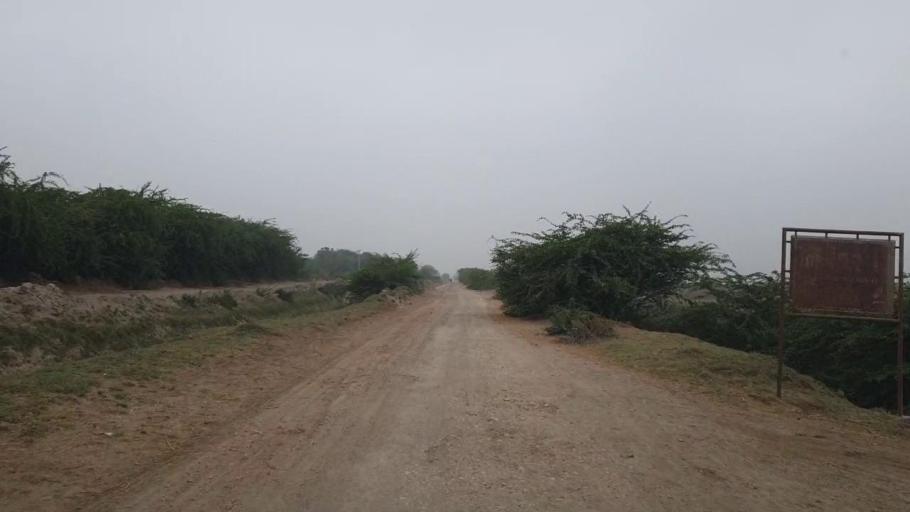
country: PK
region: Sindh
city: Badin
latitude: 24.6091
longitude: 68.6773
